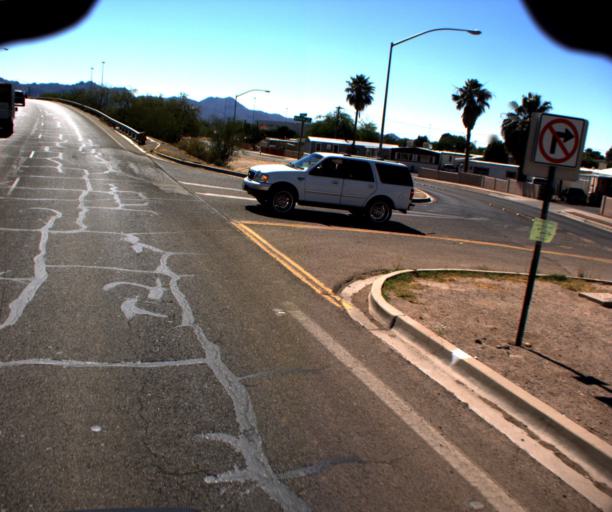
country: US
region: Arizona
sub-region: Pima County
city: Flowing Wells
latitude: 32.2613
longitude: -110.9980
